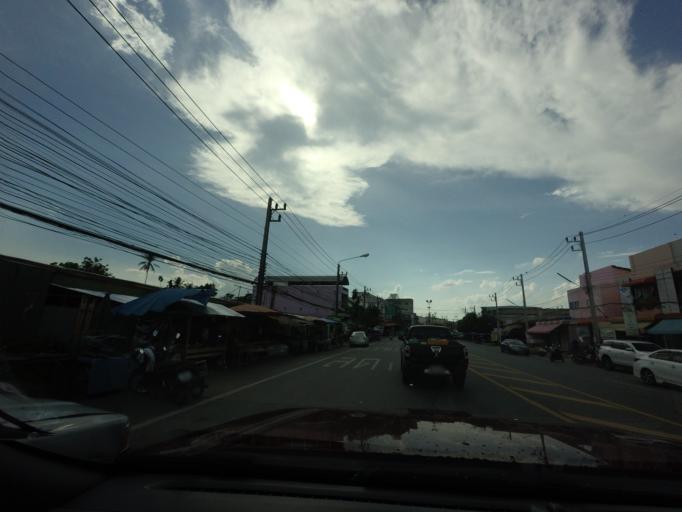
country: TH
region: Pattani
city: Khok Pho
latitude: 6.6775
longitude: 101.1469
